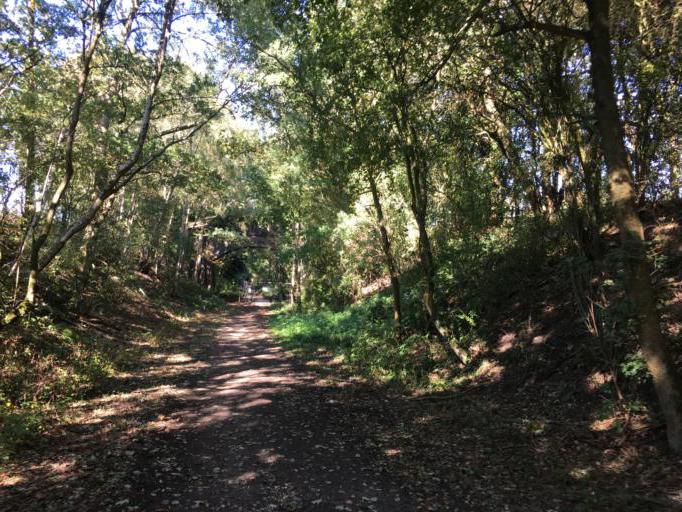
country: GB
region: England
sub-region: Solihull
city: Balsall Common
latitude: 52.3858
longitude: -1.6177
